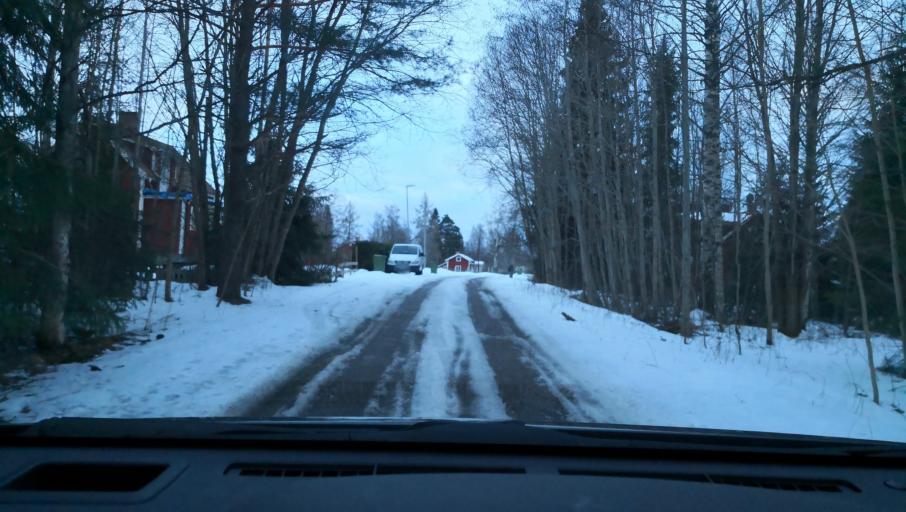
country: SE
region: Dalarna
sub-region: Smedjebackens Kommun
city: Smedjebacken
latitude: 60.0633
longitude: 15.5553
